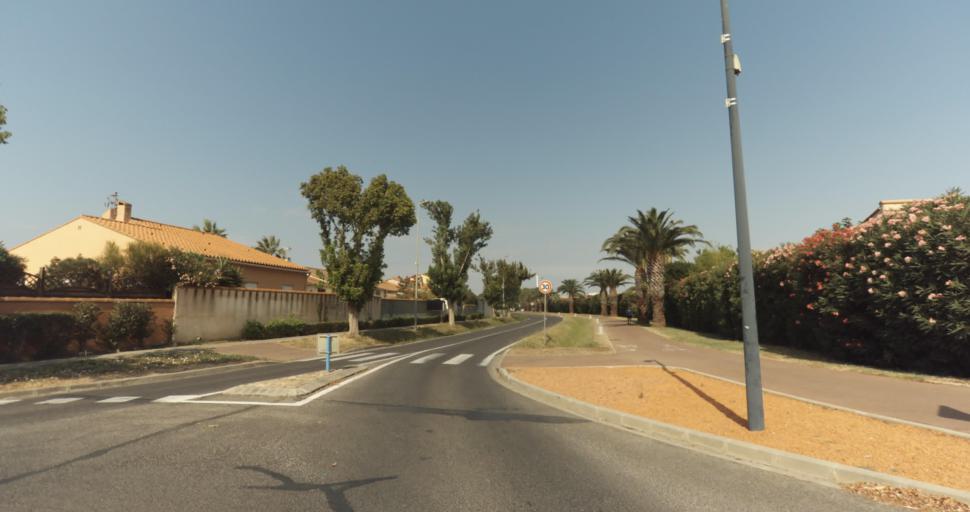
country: FR
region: Languedoc-Roussillon
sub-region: Departement des Pyrenees-Orientales
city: Latour-Bas-Elne
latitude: 42.6186
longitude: 3.0144
